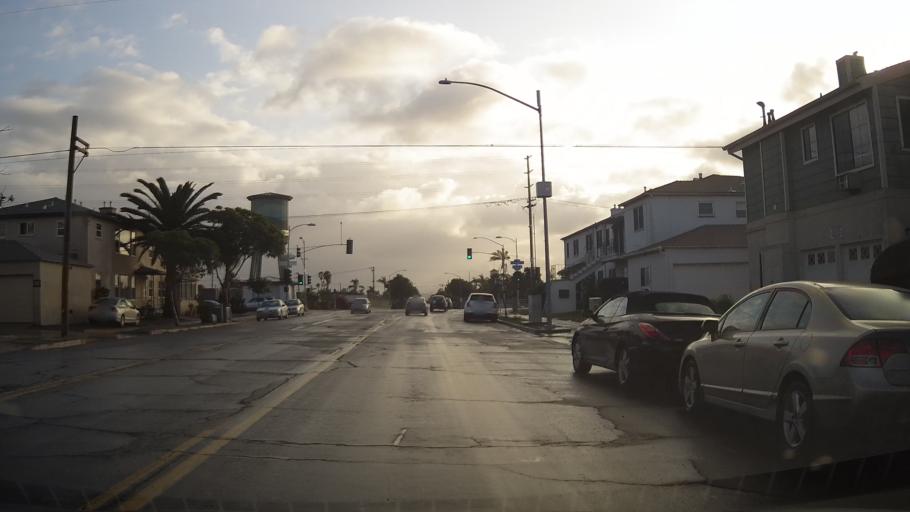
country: US
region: California
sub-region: San Diego County
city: San Diego
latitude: 32.7573
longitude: -117.1274
